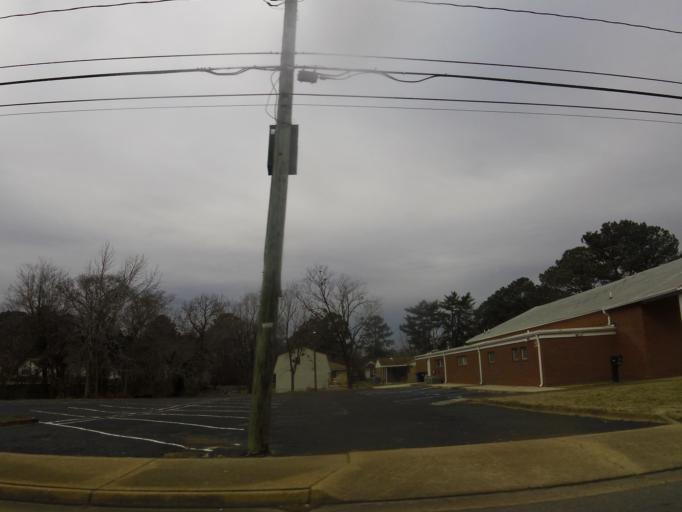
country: US
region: Virginia
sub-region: City of Portsmouth
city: Portsmouth Heights
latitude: 36.8199
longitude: -76.3529
